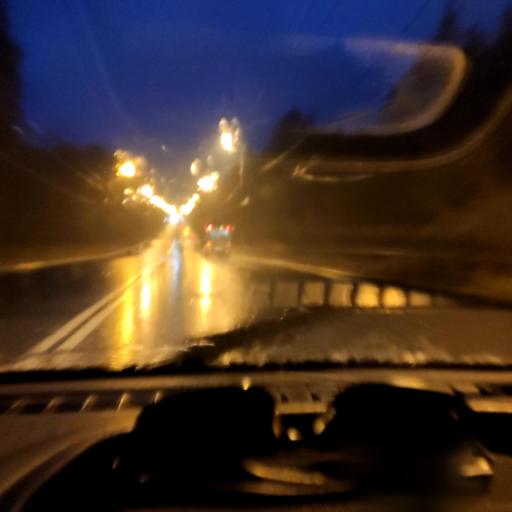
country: RU
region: Samara
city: Zhigulevsk
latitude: 53.5007
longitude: 49.4634
